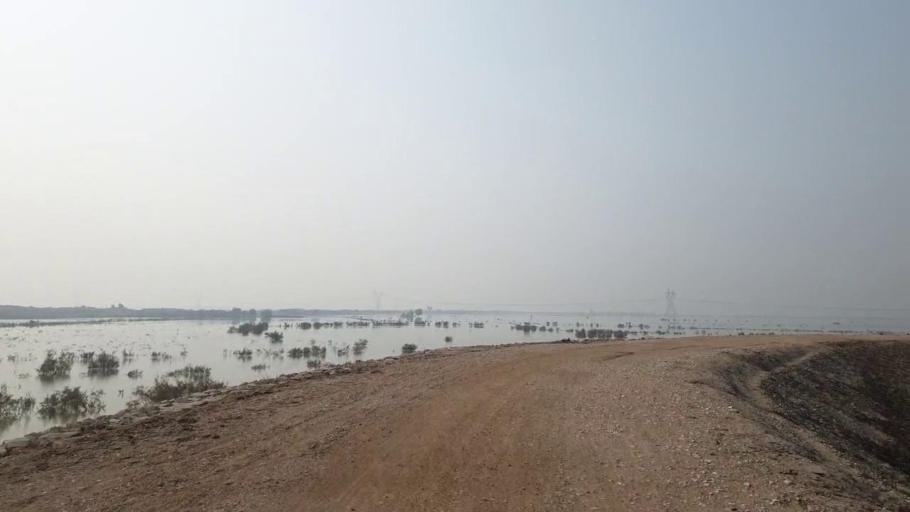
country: PK
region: Sindh
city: Sehwan
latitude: 26.3992
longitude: 67.8312
